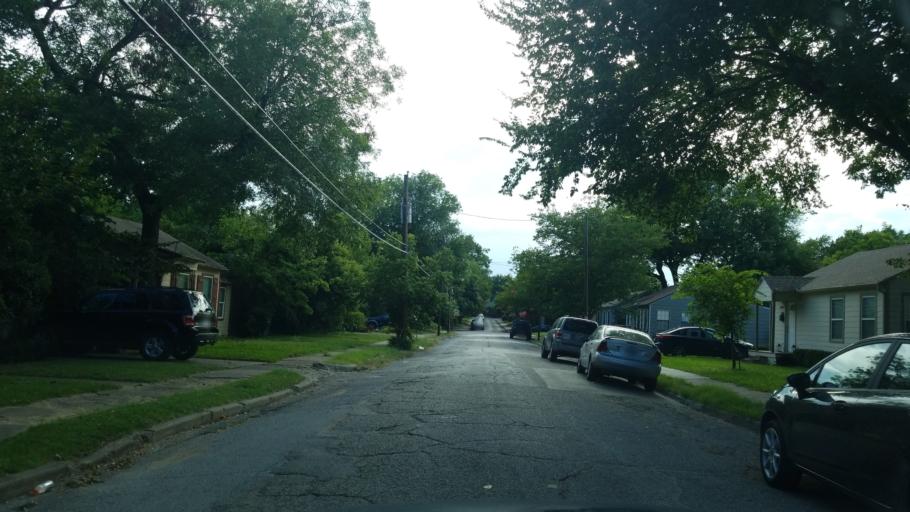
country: US
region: Texas
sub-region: Dallas County
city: Highland Park
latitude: 32.8130
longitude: -96.7659
